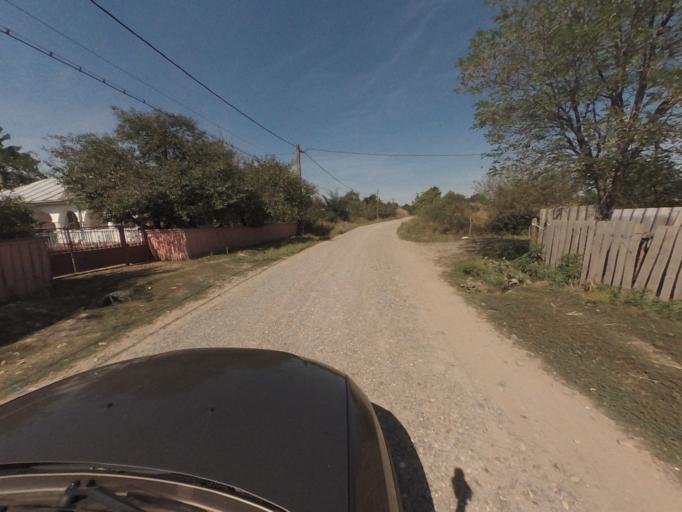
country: RO
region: Vaslui
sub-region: Comuna Deleni
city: Deleni
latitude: 46.5312
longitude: 27.7536
